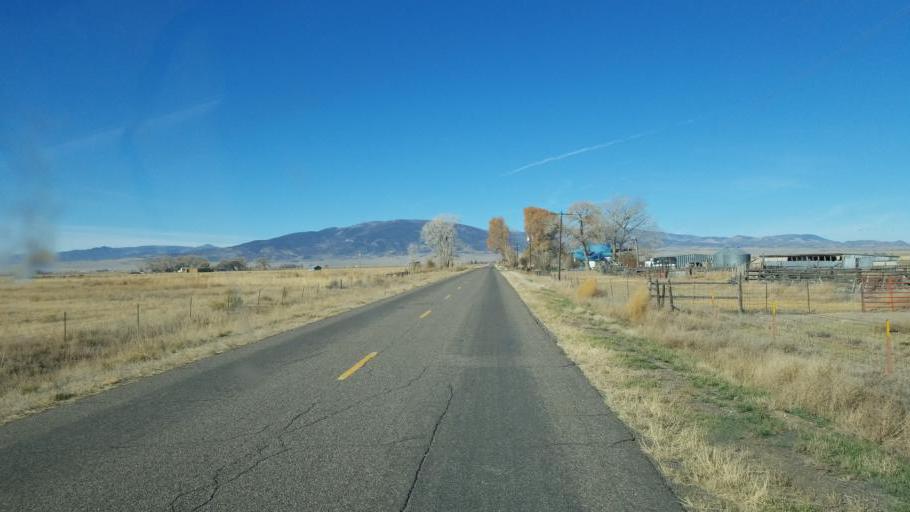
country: US
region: Colorado
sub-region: Rio Grande County
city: Monte Vista
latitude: 37.4591
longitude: -106.0820
